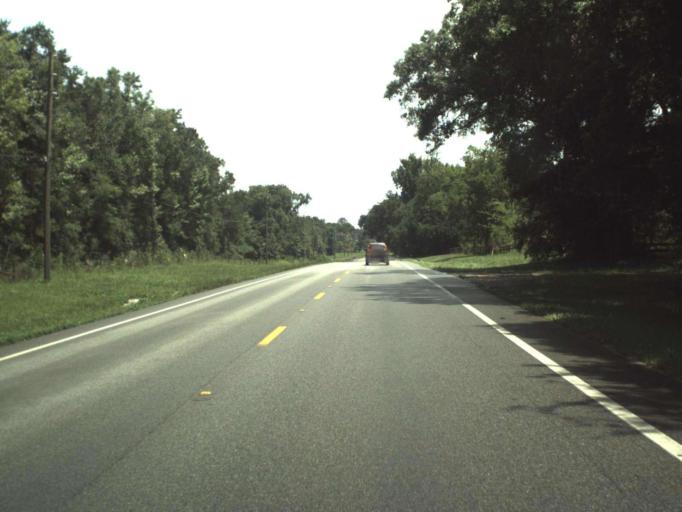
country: US
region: Florida
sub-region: Sumter County
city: Lake Panasoffkee
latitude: 28.7674
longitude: -82.0639
